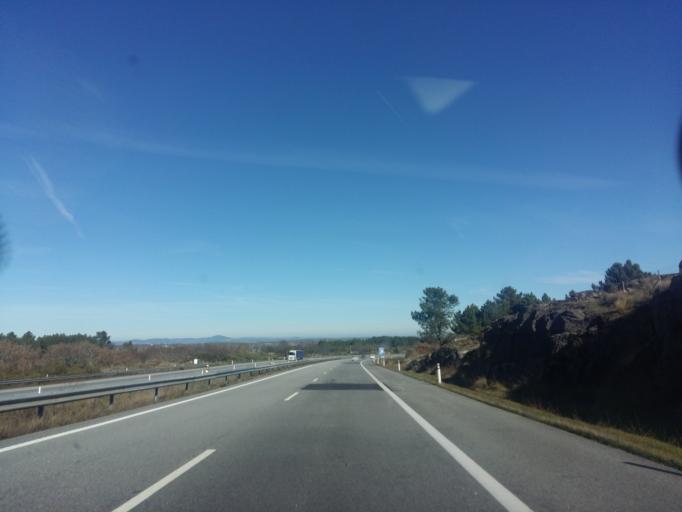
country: PT
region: Guarda
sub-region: Guarda
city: Sequeira
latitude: 40.5968
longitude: -7.1323
